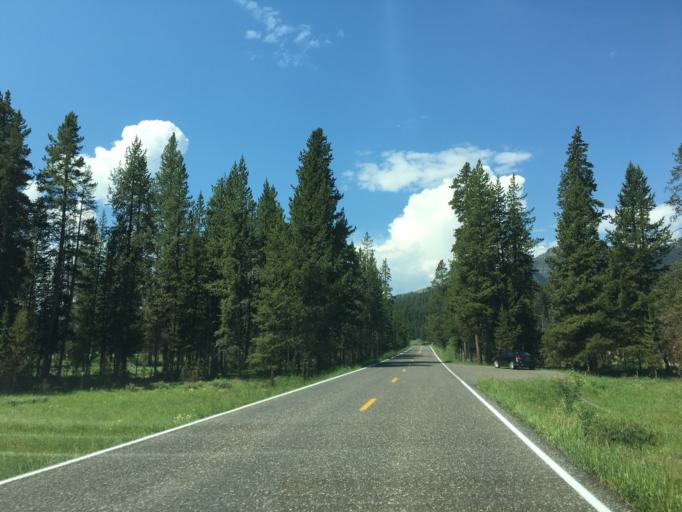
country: US
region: Montana
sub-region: Park County
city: Livingston
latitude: 44.9162
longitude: -110.1087
